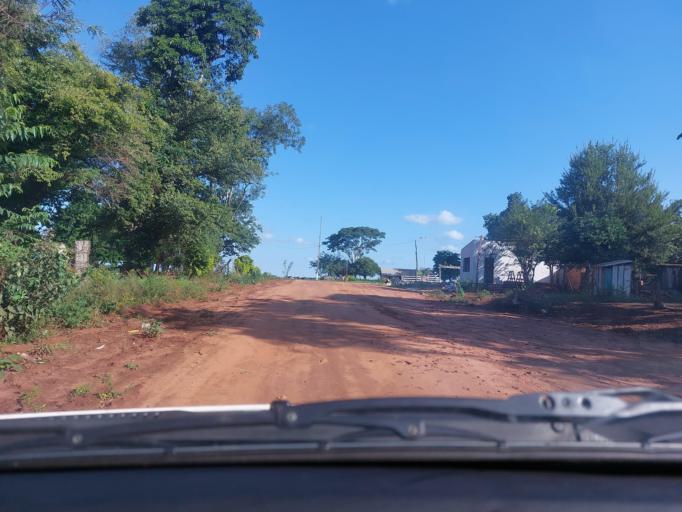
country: PY
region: San Pedro
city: Guayaybi
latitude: -24.5309
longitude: -56.5455
